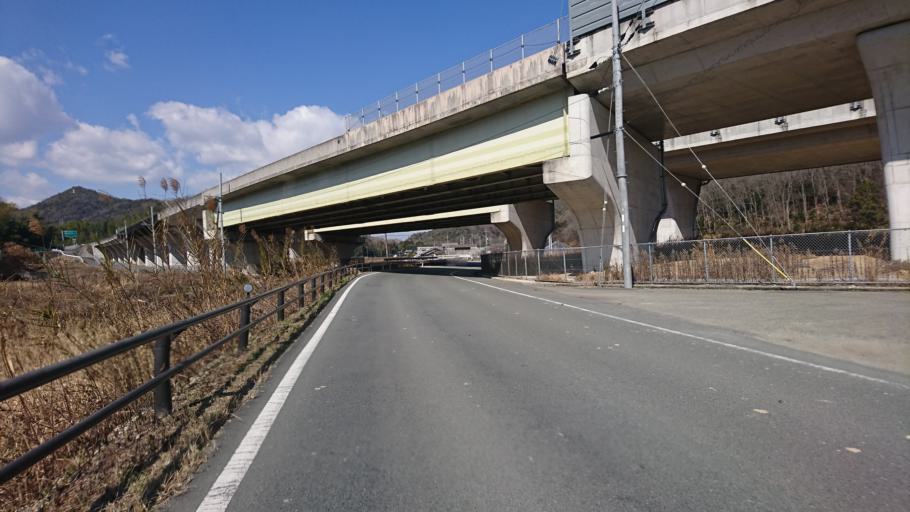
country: JP
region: Hyogo
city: Kakogawacho-honmachi
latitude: 34.8480
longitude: 134.8123
